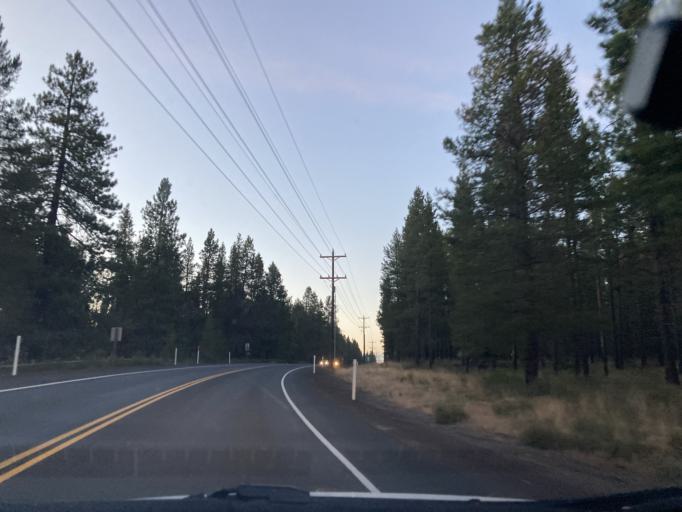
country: US
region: Oregon
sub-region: Deschutes County
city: Three Rivers
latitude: 43.8335
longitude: -121.4420
